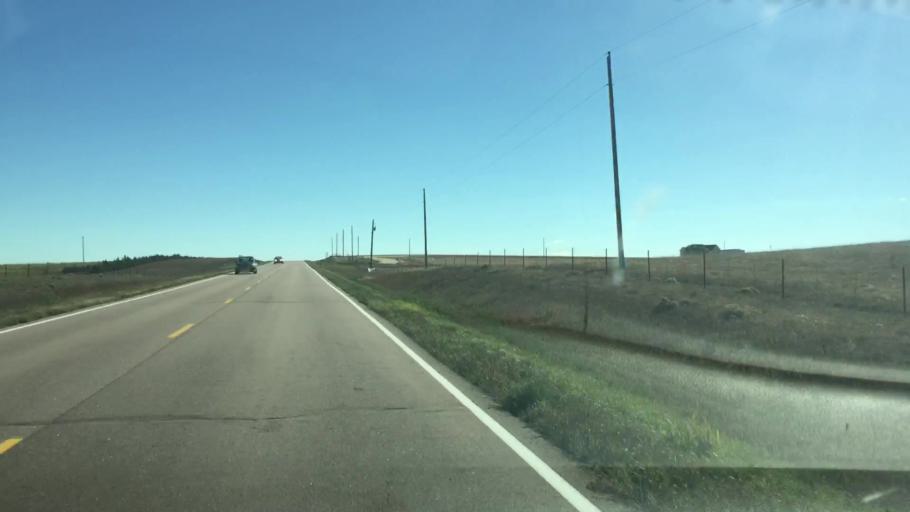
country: US
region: Colorado
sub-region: Lincoln County
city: Limon
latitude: 39.2735
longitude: -104.0260
